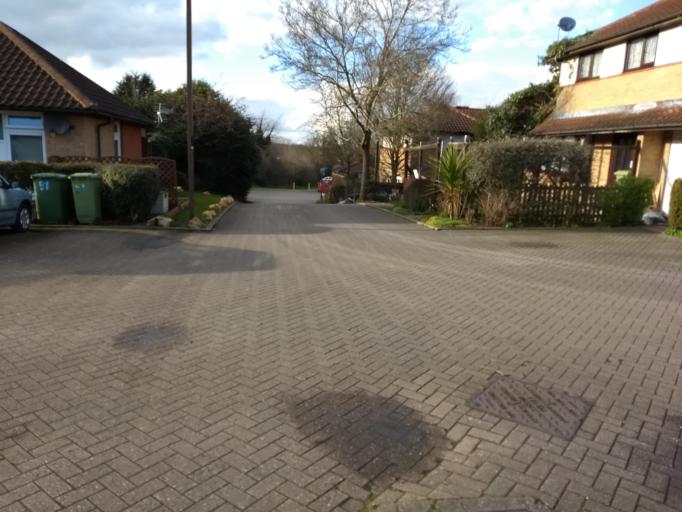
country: GB
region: England
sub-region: Milton Keynes
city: Milton Keynes
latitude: 52.0566
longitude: -0.7414
